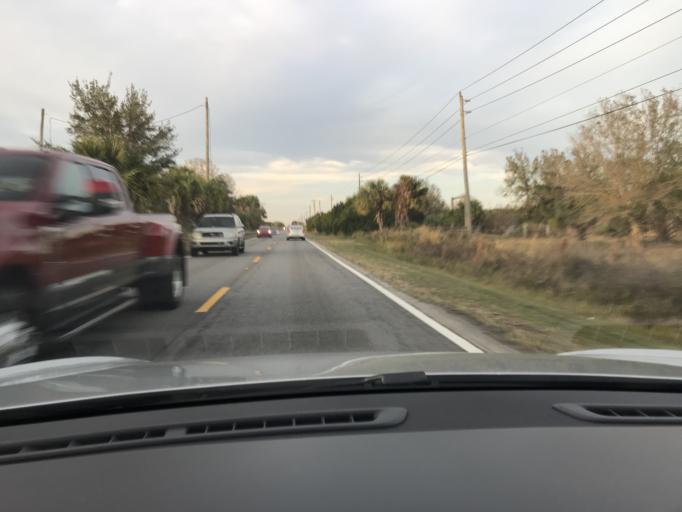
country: US
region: Florida
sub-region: Saint Lucie County
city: Lakewood Park
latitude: 27.5465
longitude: -80.4309
